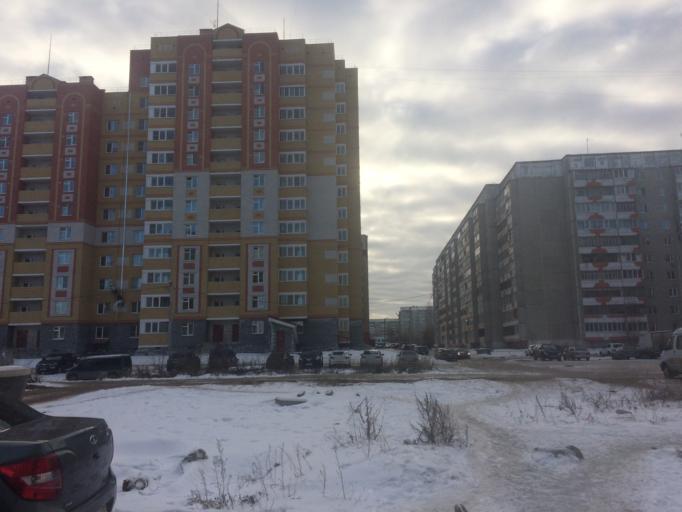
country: RU
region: Mariy-El
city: Yoshkar-Ola
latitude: 56.6389
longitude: 47.9289
